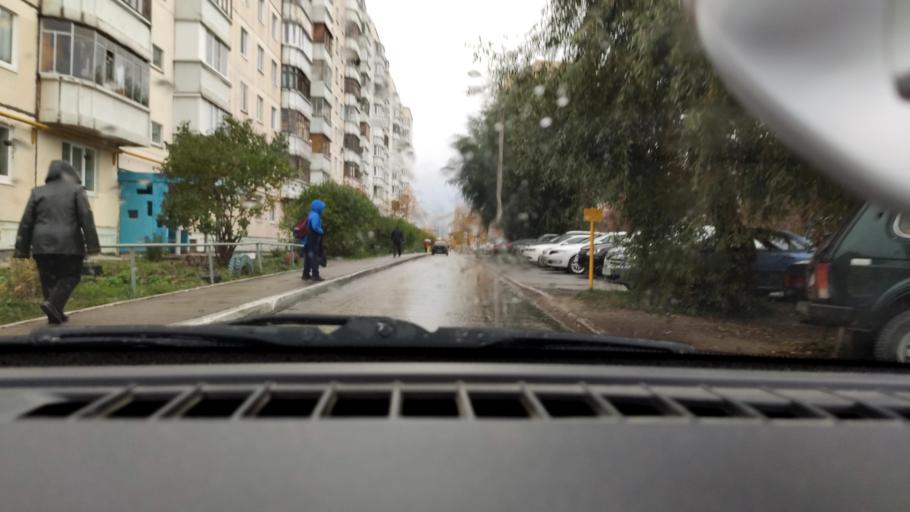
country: RU
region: Perm
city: Perm
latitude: 57.9742
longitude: 56.2013
